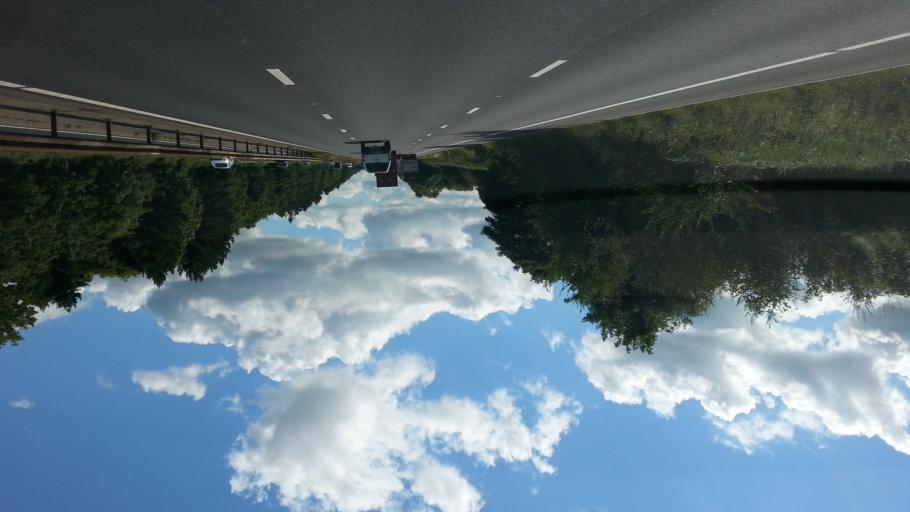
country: GB
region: England
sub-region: Leicestershire
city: Broughton Astley
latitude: 52.5105
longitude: -1.1825
